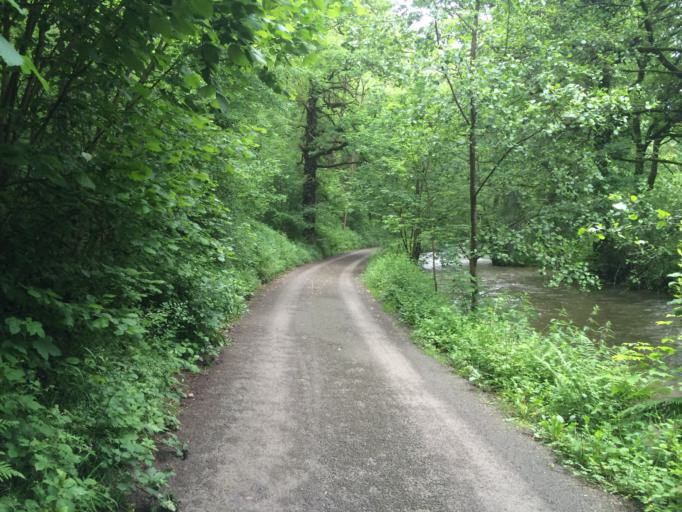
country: BE
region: Wallonia
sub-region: Province de Namur
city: Yvoir
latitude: 50.3238
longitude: 4.9473
